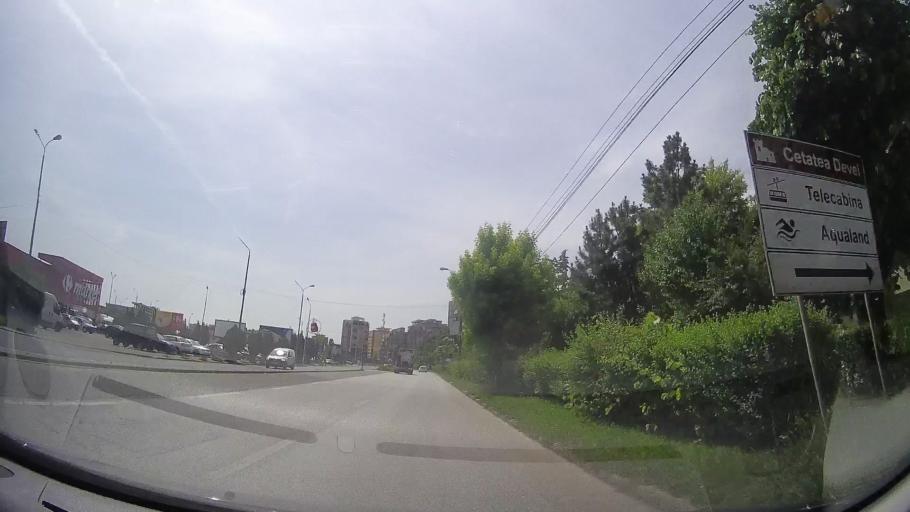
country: RO
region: Hunedoara
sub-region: Municipiul Deva
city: Deva
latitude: 45.8857
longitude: 22.9078
